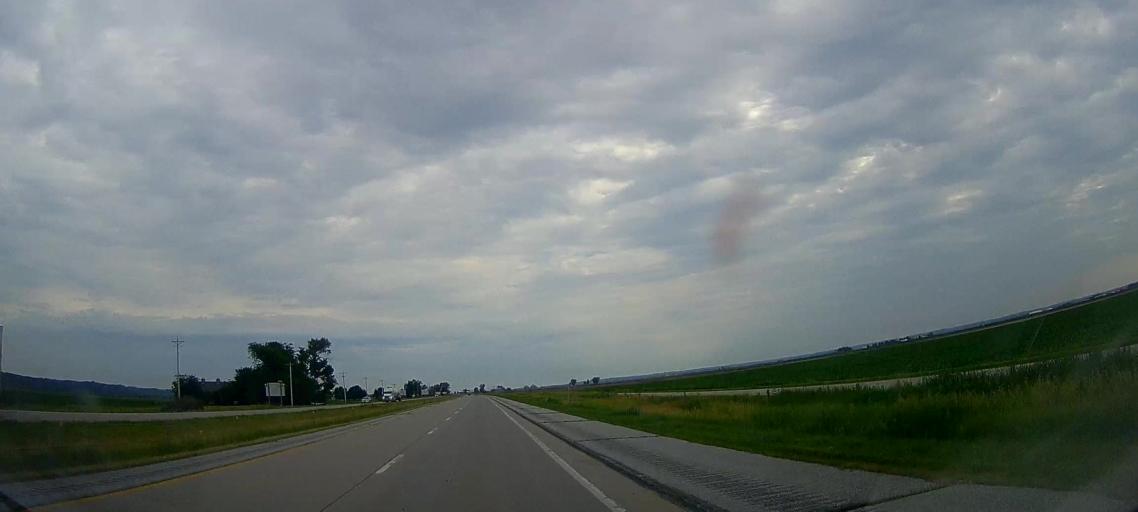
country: US
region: Iowa
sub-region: Harrison County
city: Missouri Valley
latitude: 41.5375
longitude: -95.9179
